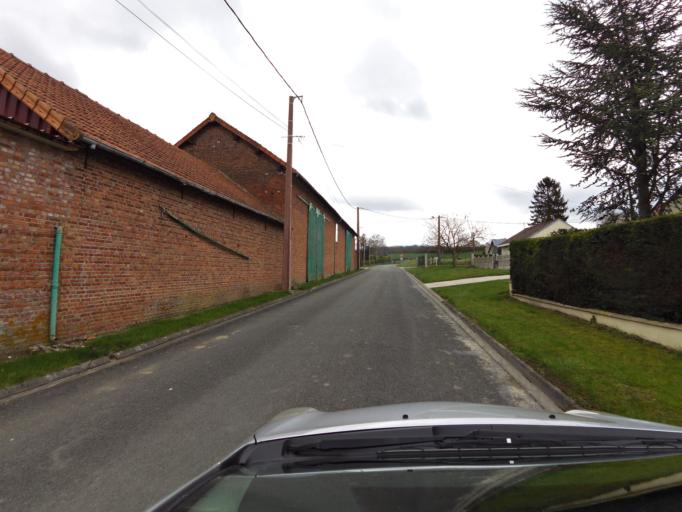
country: FR
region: Picardie
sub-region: Departement de la Somme
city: Bray-sur-Somme
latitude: 49.9394
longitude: 2.8180
